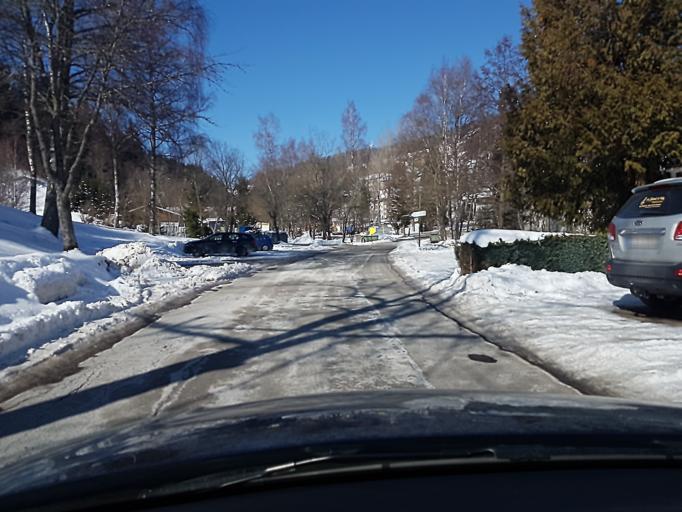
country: DE
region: Baden-Wuerttemberg
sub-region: Freiburg Region
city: Triberg im Schwarzwald
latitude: 48.1373
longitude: 8.2132
